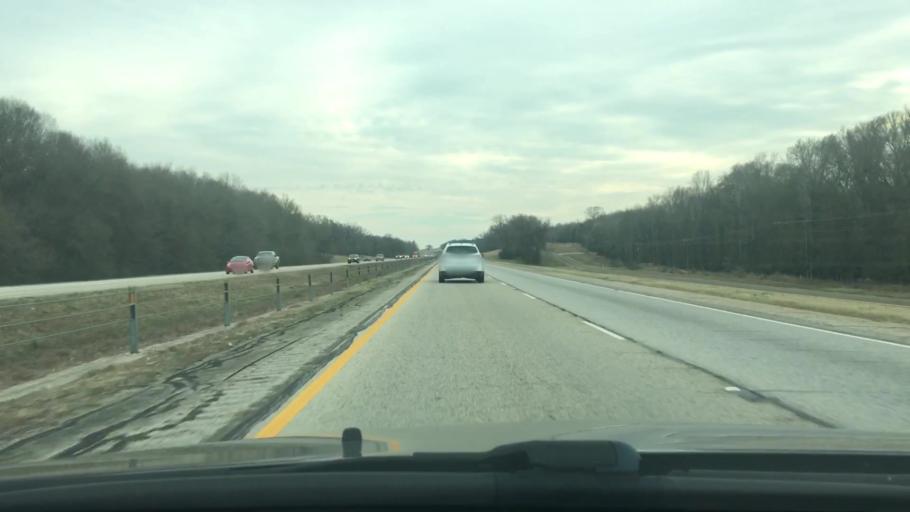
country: US
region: Texas
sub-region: Leon County
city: Centerville
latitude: 31.3059
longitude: -96.0014
